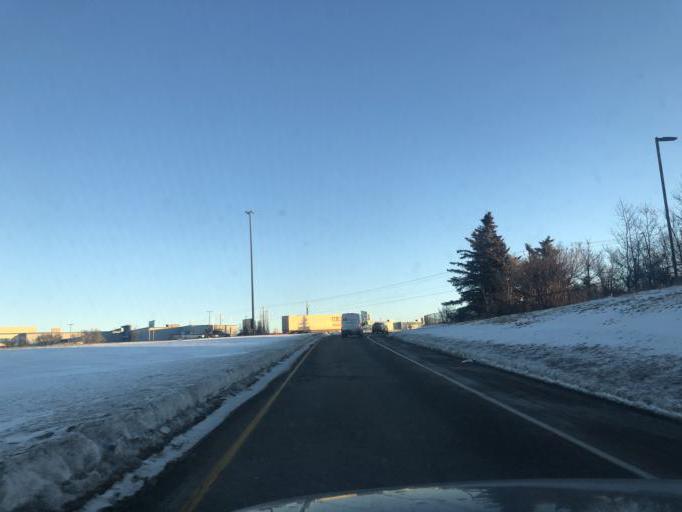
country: CA
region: Alberta
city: Calgary
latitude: 51.0951
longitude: -114.0380
